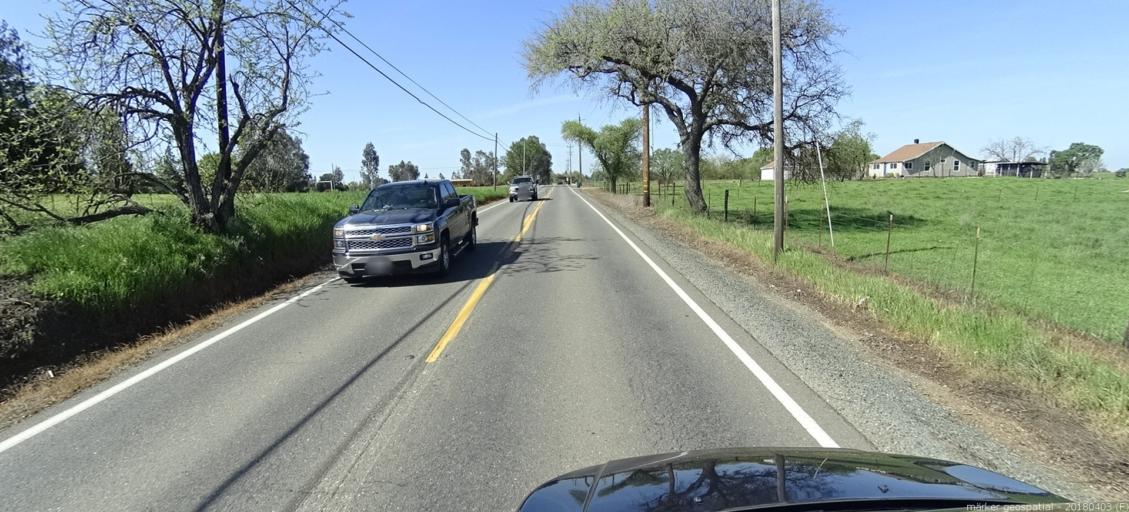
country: US
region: California
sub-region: Sacramento County
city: Wilton
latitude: 38.4222
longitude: -121.2165
